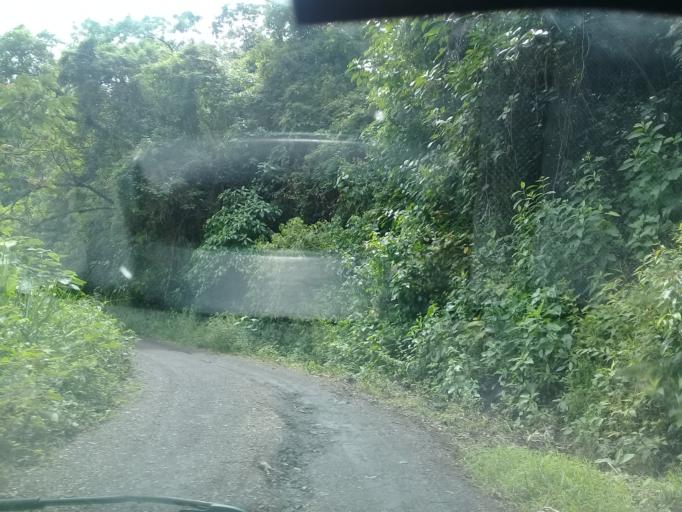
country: CO
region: Cundinamarca
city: Quipile
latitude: 4.7153
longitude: -74.5489
